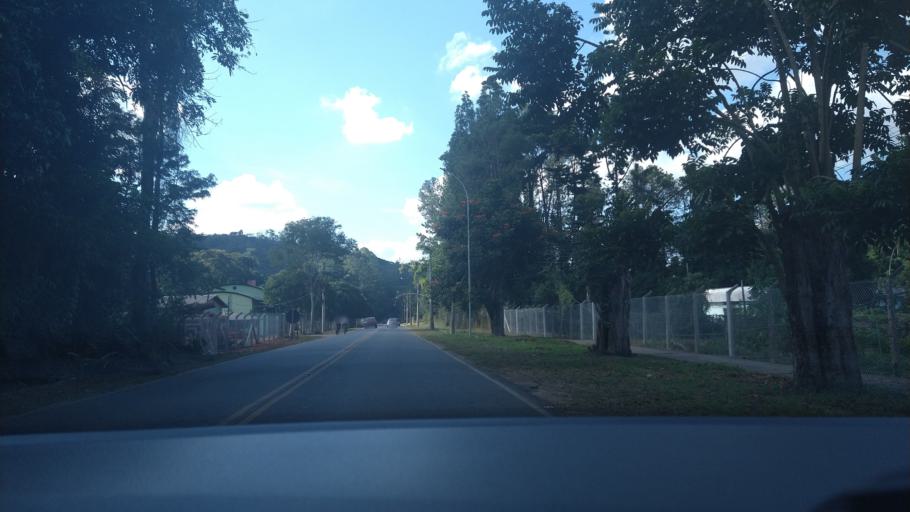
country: BR
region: Minas Gerais
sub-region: Vicosa
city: Vicosa
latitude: -20.7732
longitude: -42.8766
